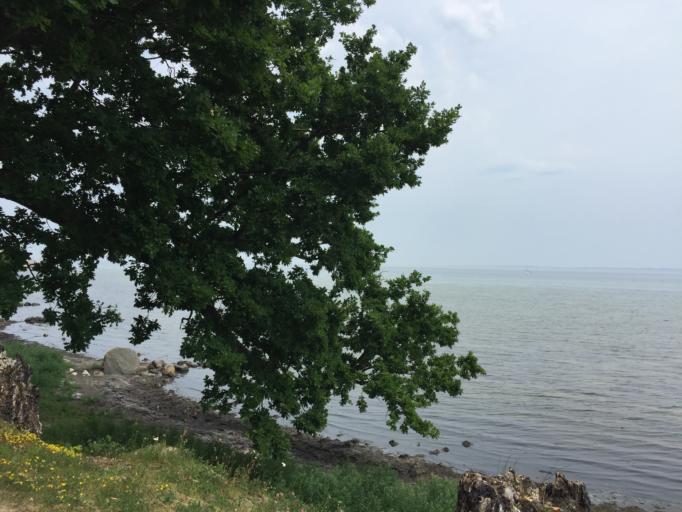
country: DK
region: South Denmark
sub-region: Svendborg Kommune
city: Thuro By
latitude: 55.1339
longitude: 10.7794
